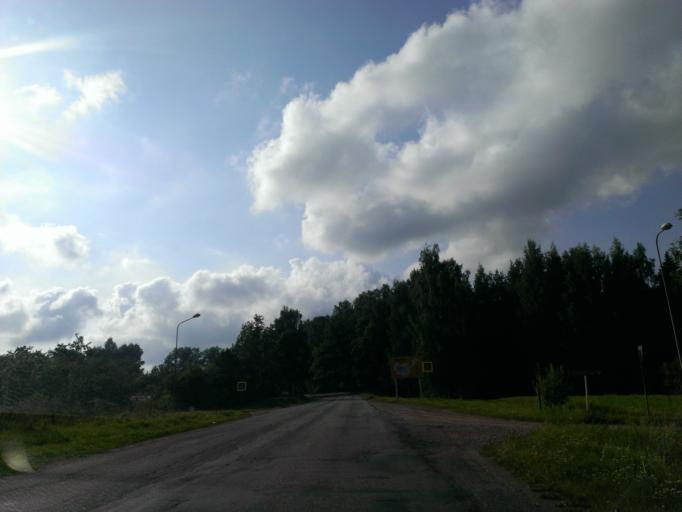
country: LV
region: Priekuli
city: Priekuli
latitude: 57.3153
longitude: 25.3724
